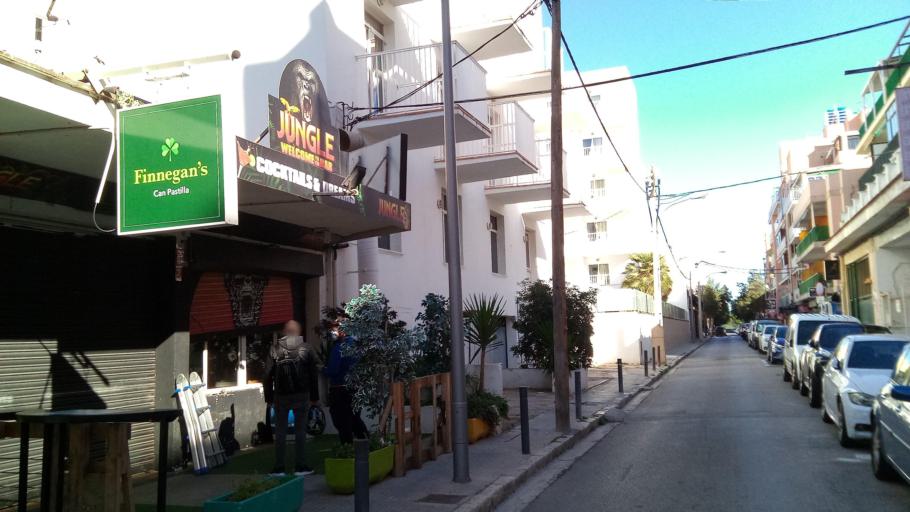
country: ES
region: Balearic Islands
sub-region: Illes Balears
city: s'Arenal
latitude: 39.5339
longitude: 2.7165
